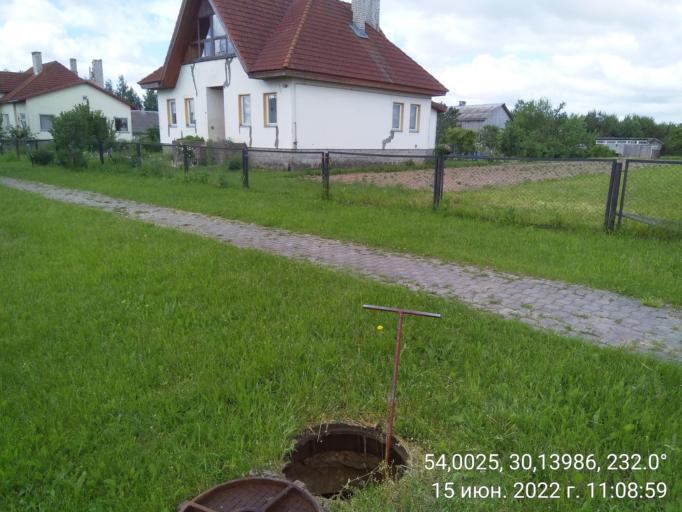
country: BY
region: Mogilev
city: Vishow
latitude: 54.0025
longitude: 30.1399
